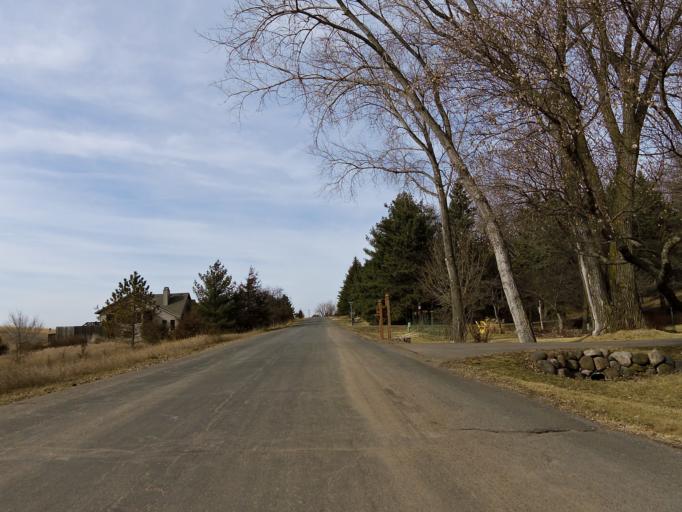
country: US
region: Minnesota
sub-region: Washington County
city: Lakeland
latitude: 44.9461
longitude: -92.7830
